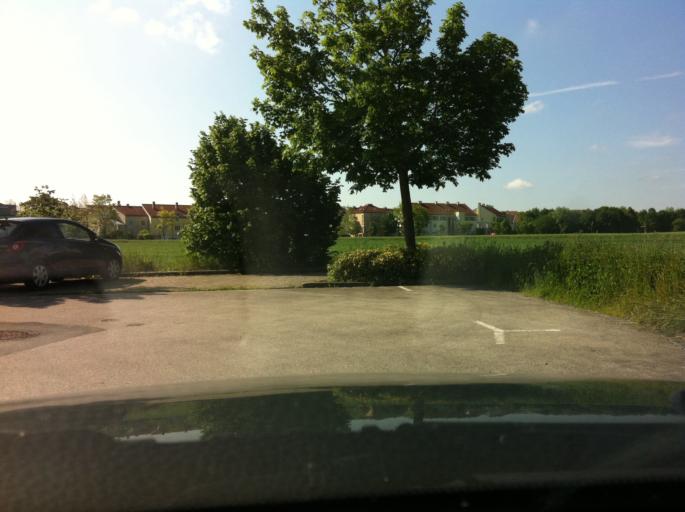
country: DE
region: Bavaria
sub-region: Upper Bavaria
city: Taufkirchen
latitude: 48.0499
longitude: 11.6119
